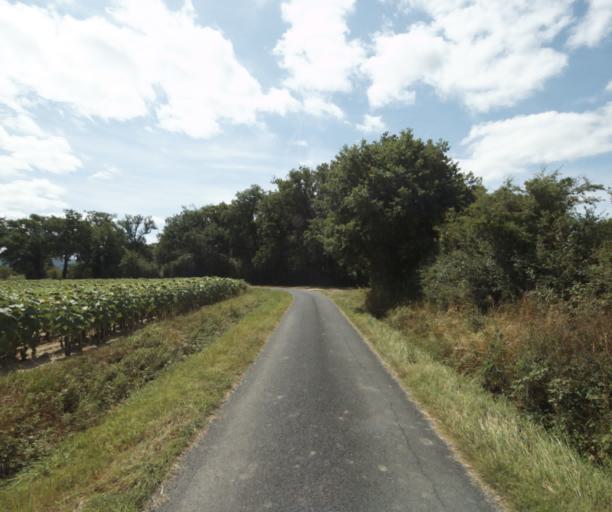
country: FR
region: Midi-Pyrenees
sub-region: Departement du Tarn
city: Soreze
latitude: 43.4981
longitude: 2.0654
